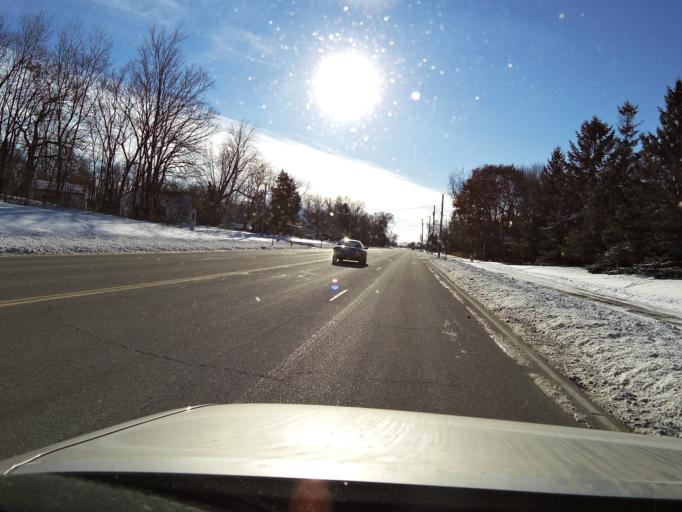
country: US
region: Minnesota
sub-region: Ramsey County
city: Maplewood
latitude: 44.9673
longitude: -93.0007
